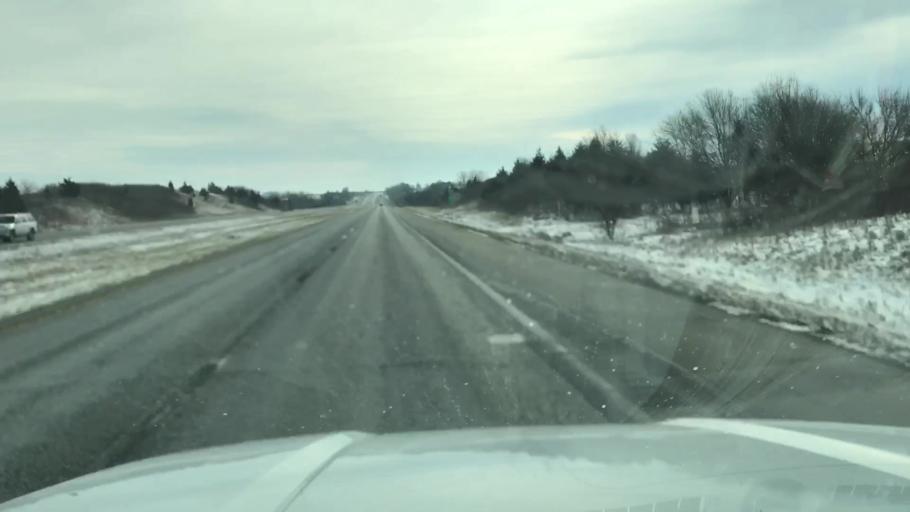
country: US
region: Missouri
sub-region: Holt County
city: Oregon
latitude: 40.0229
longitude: -95.0992
